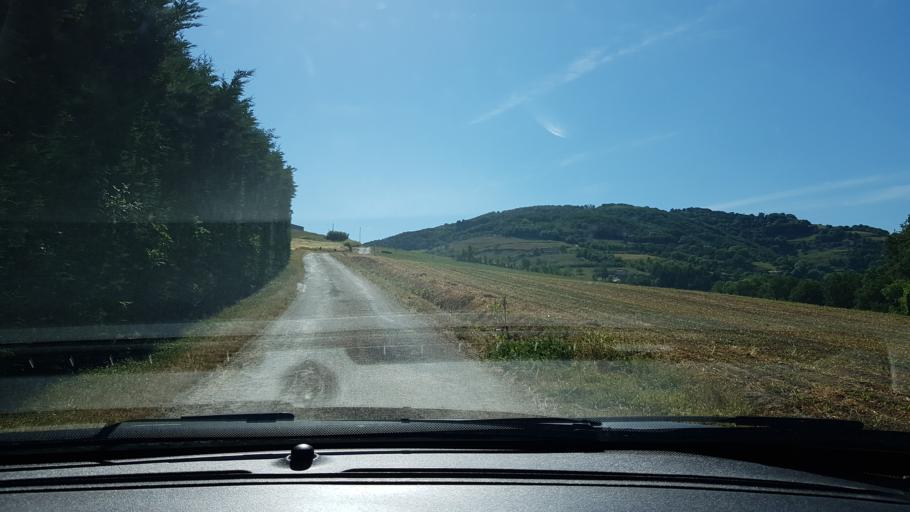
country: FR
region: Rhone-Alpes
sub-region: Departement du Rhone
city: Saint-Didier-sous-Riverie
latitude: 45.5852
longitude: 4.6011
